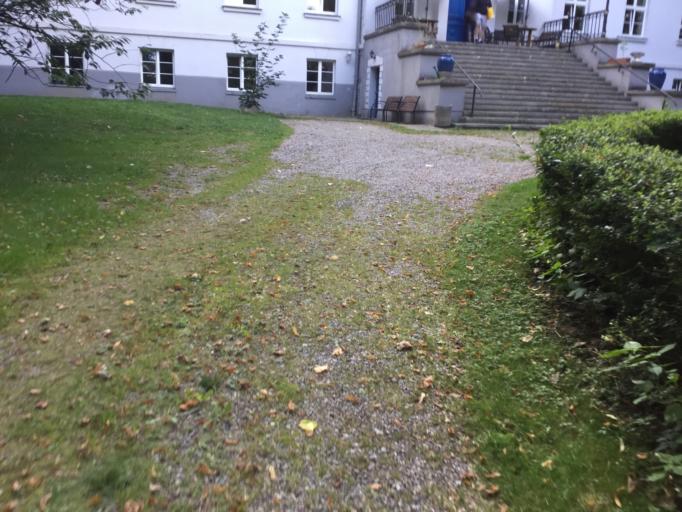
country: DE
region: Mecklenburg-Vorpommern
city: Jordenstorf
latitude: 53.8260
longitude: 12.6946
